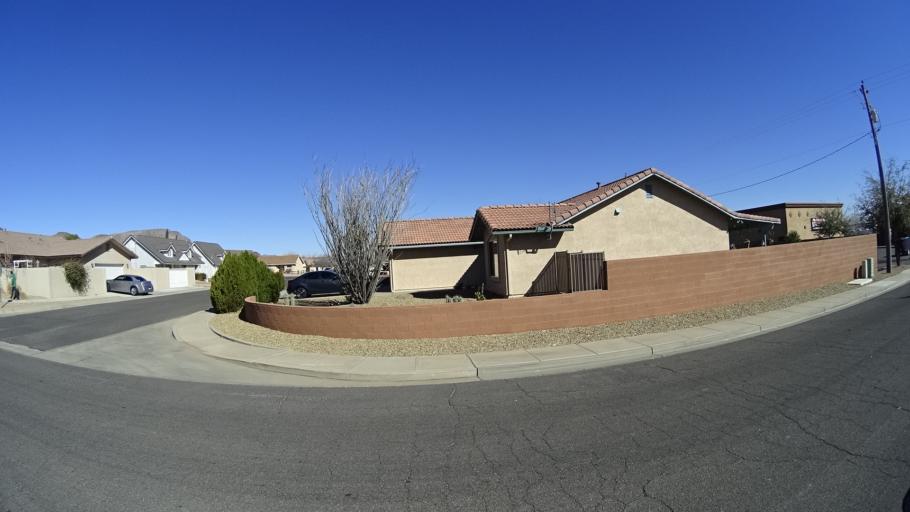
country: US
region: Arizona
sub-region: Mohave County
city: New Kingman-Butler
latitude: 35.2321
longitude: -114.0383
